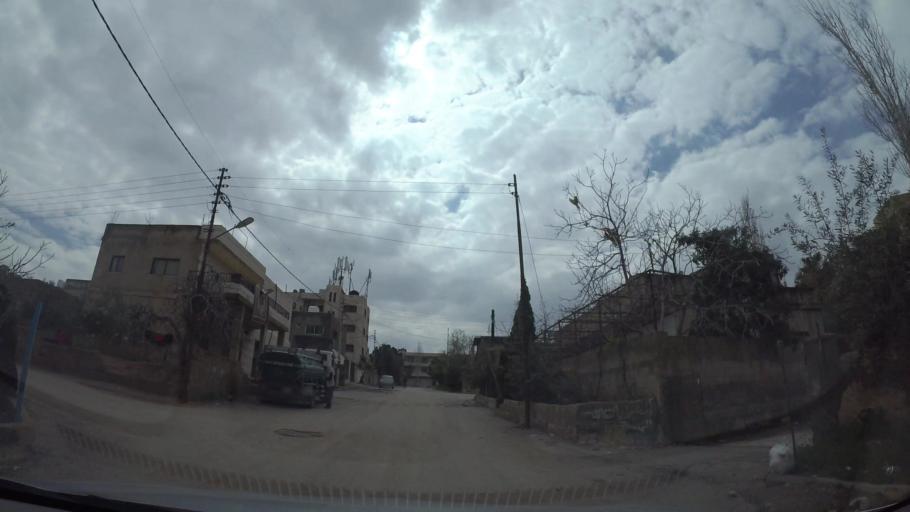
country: JO
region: Amman
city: Al Jubayhah
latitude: 32.0544
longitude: 35.8322
